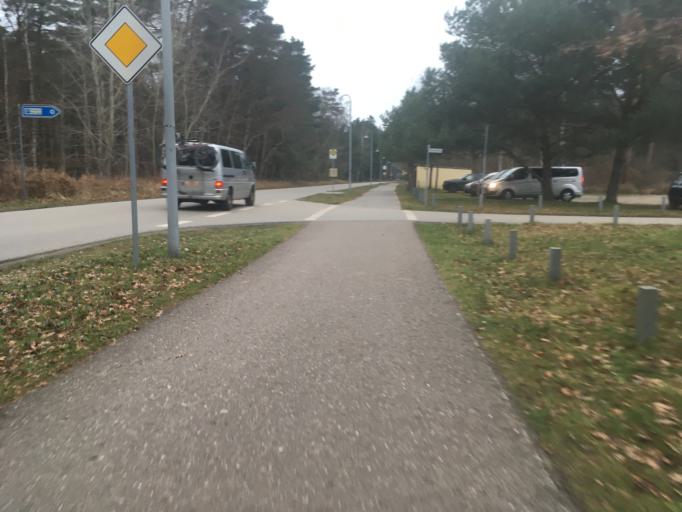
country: DE
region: Mecklenburg-Vorpommern
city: Ostseebad Binz
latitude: 54.4465
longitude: 13.5665
